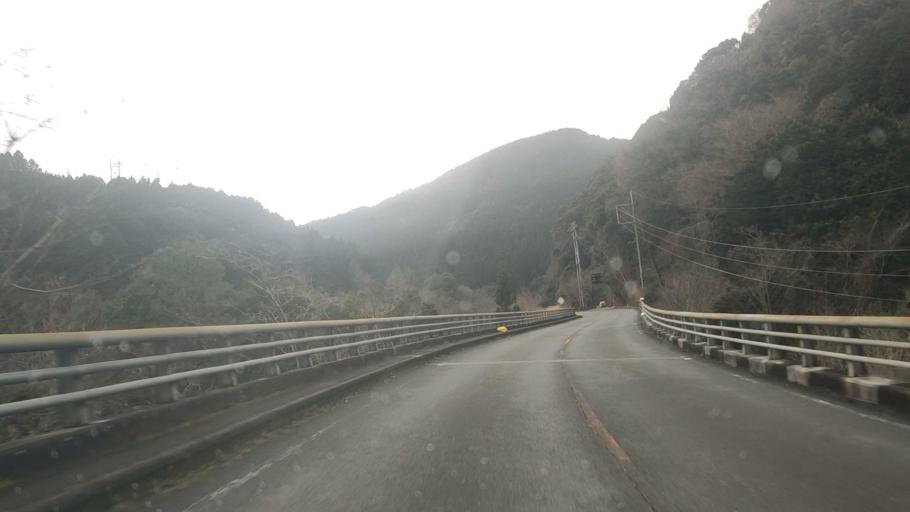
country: JP
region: Kumamoto
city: Hitoyoshi
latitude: 32.1238
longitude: 130.8117
